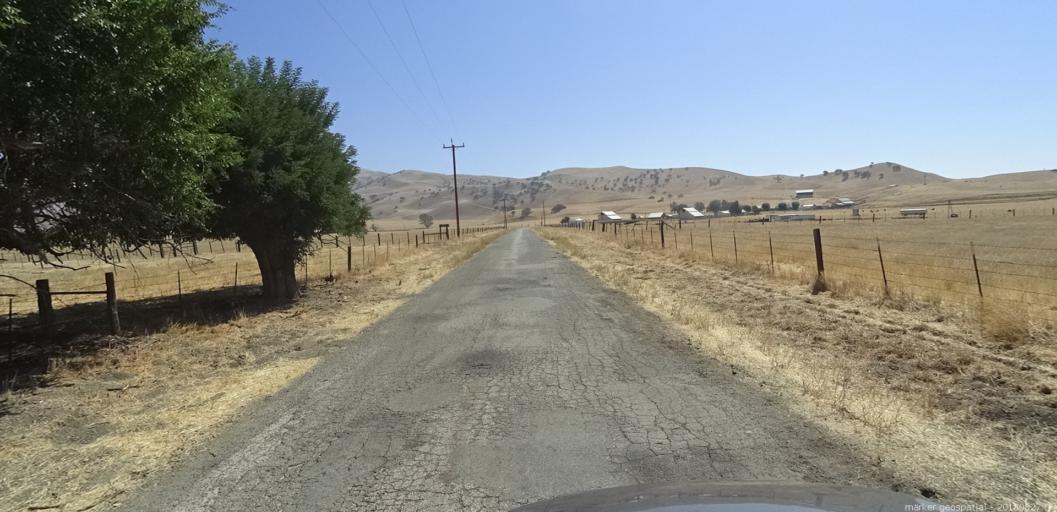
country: US
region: California
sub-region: Monterey County
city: King City
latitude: 36.2801
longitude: -120.9491
